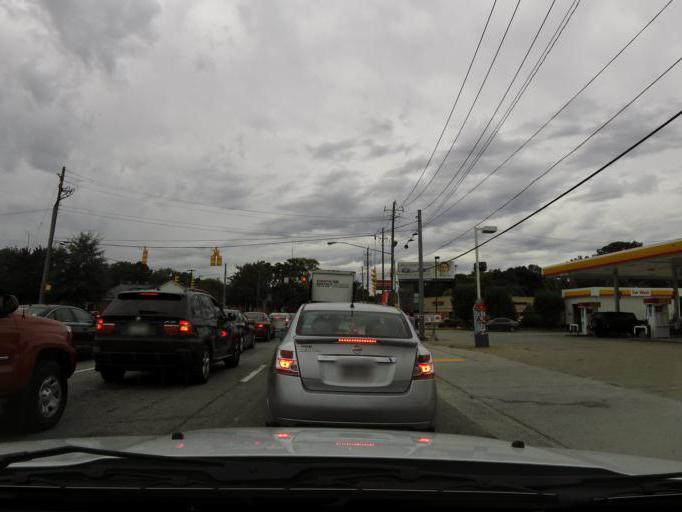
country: US
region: Georgia
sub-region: Fulton County
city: Atlanta
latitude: 33.8036
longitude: -84.4142
